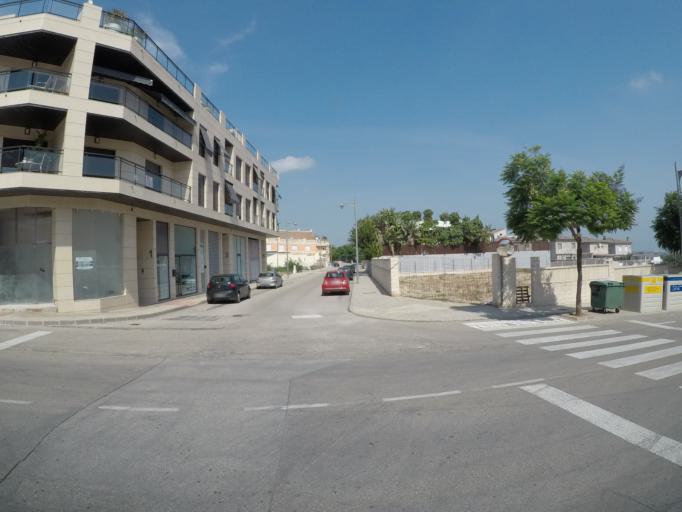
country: ES
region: Valencia
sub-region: Provincia de Alicante
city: Pego
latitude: 38.8429
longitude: -0.1131
